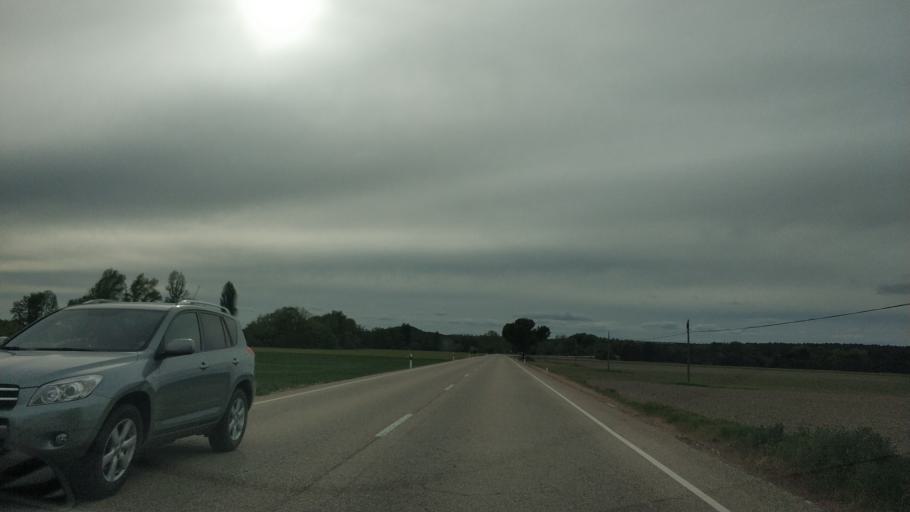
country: ES
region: Castille and Leon
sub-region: Provincia de Soria
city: Bayubas de Abajo
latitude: 41.4991
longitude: -2.8812
